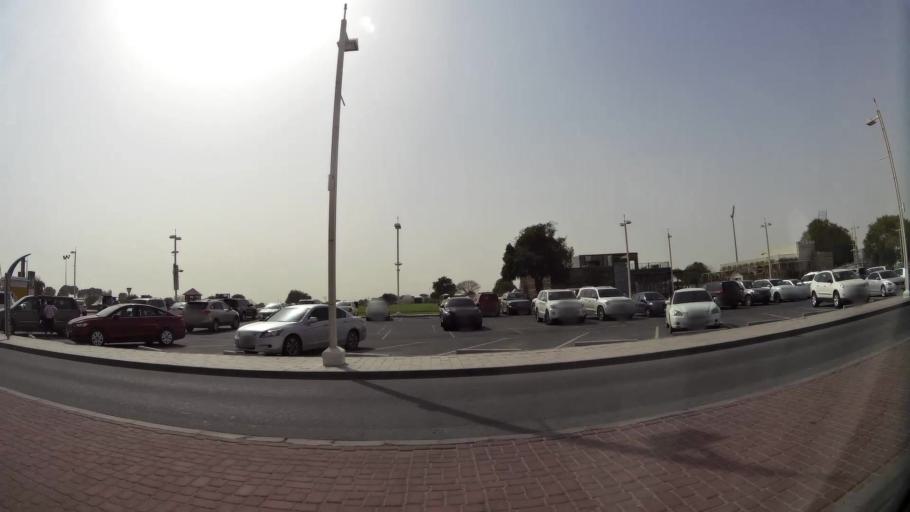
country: QA
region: Baladiyat ar Rayyan
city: Ar Rayyan
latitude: 25.2612
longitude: 51.4402
